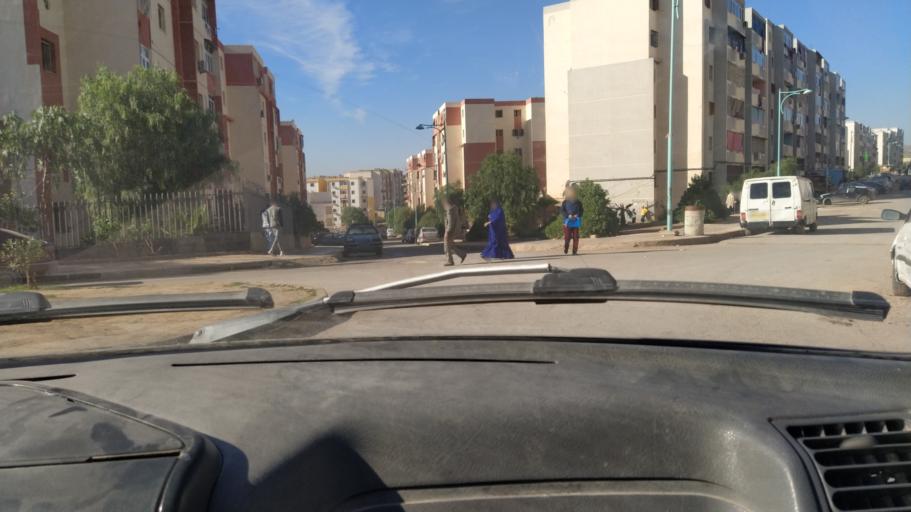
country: DZ
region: Constantine
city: Ain Smara
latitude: 36.2506
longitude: 6.5571
